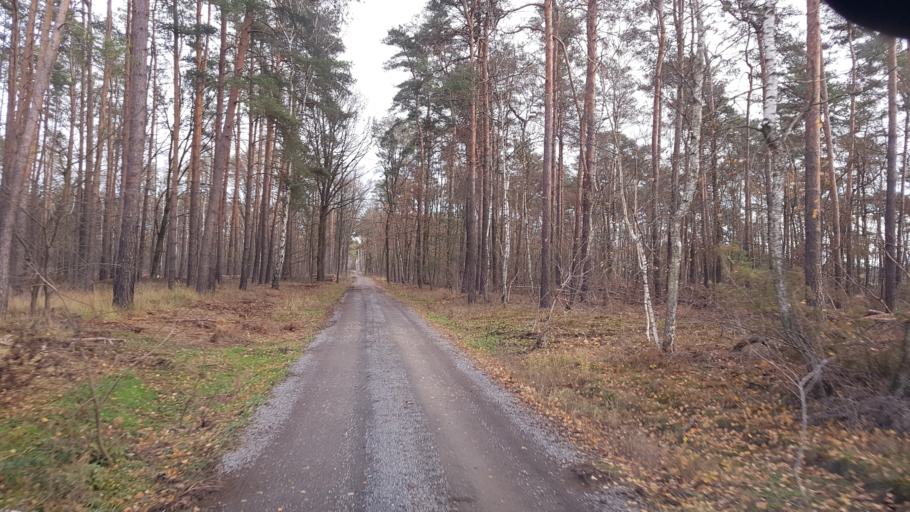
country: DE
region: Brandenburg
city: Falkenberg
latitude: 51.5732
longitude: 13.2688
